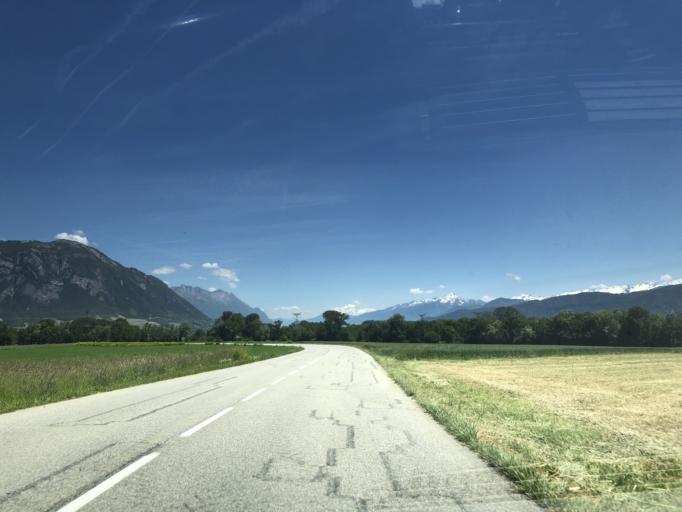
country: FR
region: Rhone-Alpes
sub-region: Departement de l'Isere
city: Chapareillan
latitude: 45.4693
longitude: 6.0040
